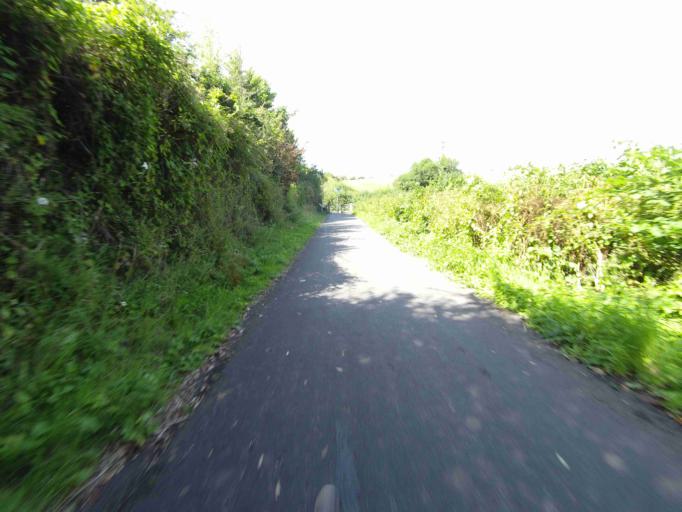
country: GB
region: England
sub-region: Devon
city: Starcross
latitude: 50.6437
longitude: -3.4280
